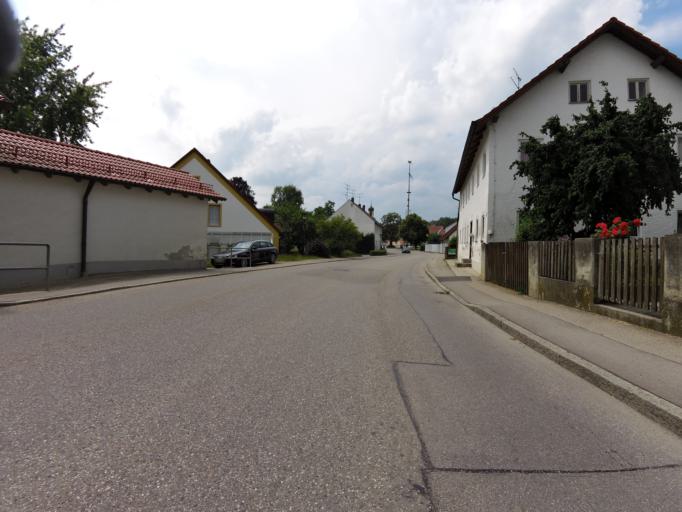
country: DE
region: Bavaria
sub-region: Upper Bavaria
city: Haag an der Amper
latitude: 48.4584
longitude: 11.8345
